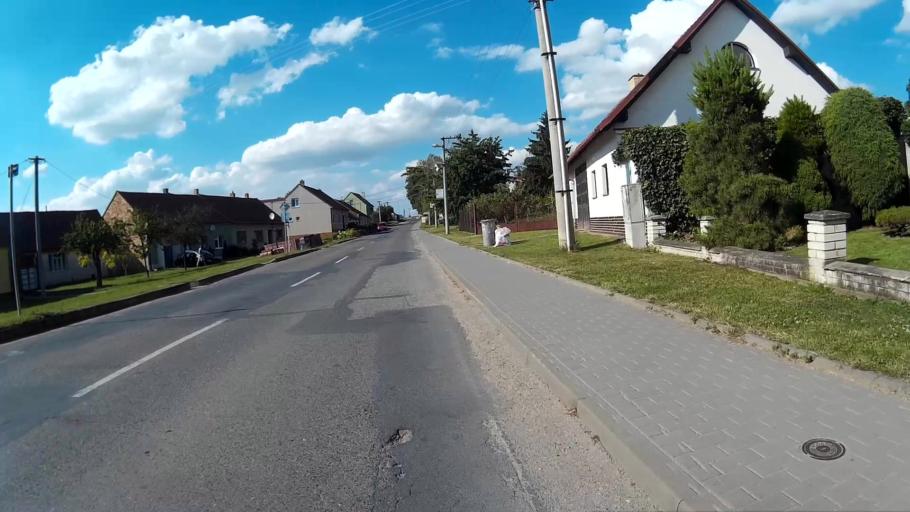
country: CZ
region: South Moravian
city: Sitborice
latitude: 49.0170
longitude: 16.7759
